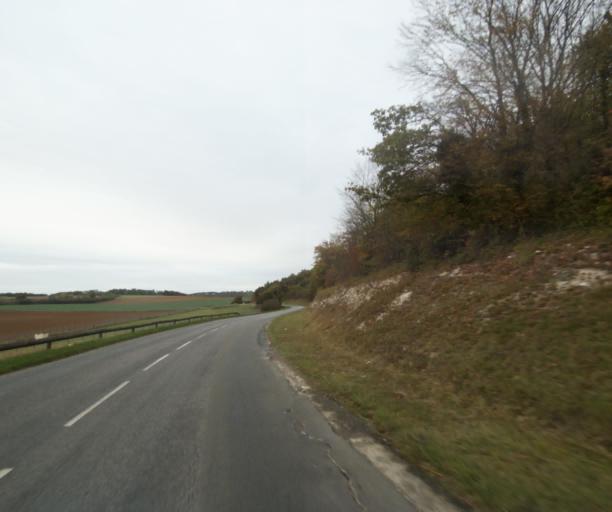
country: FR
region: Centre
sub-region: Departement d'Eure-et-Loir
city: Vert-en-Drouais
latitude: 48.7507
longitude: 1.3120
